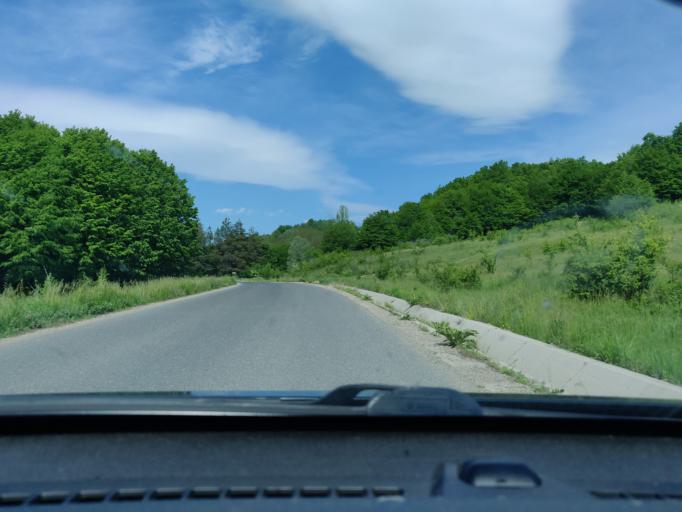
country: RO
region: Vrancea
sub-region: Comuna Vidra
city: Vidra
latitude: 45.9315
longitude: 26.8910
